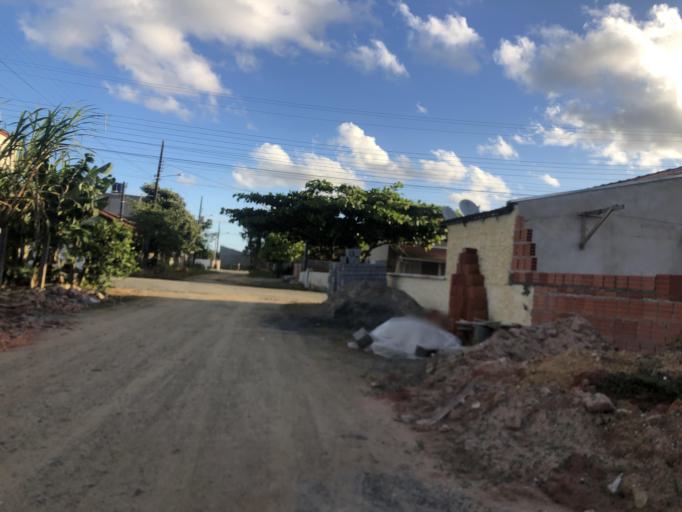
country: BR
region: Santa Catarina
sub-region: Sao Francisco Do Sul
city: Sao Francisco do Sul
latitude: -26.2197
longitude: -48.5329
